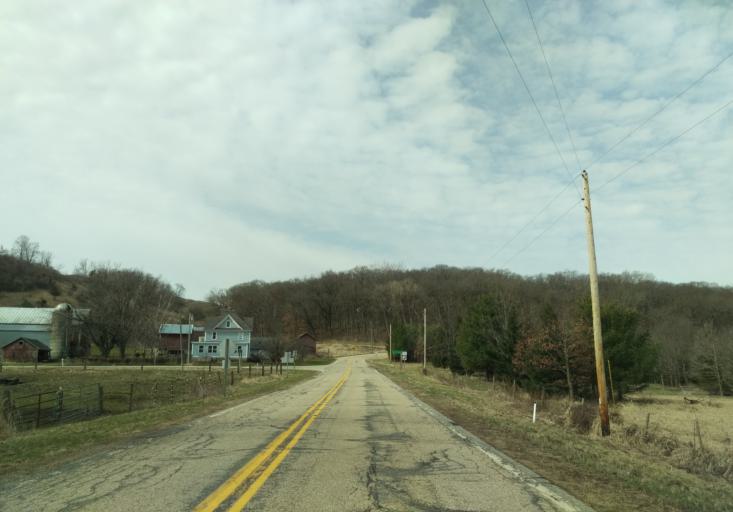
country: US
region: Wisconsin
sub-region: Dane County
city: Black Earth
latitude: 43.0702
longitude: -89.7962
